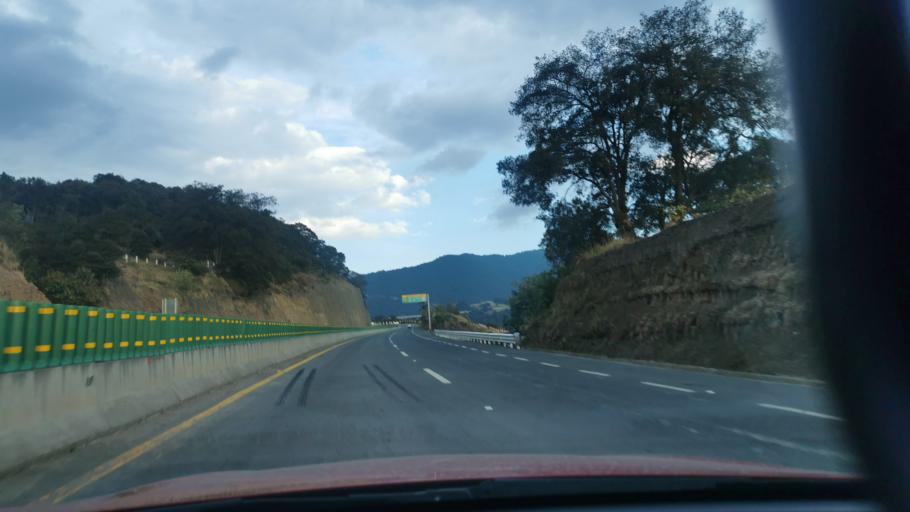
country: MX
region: Mexico
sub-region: Lerma
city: Colonia Agricola Analco
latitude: 19.3572
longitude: -99.4728
